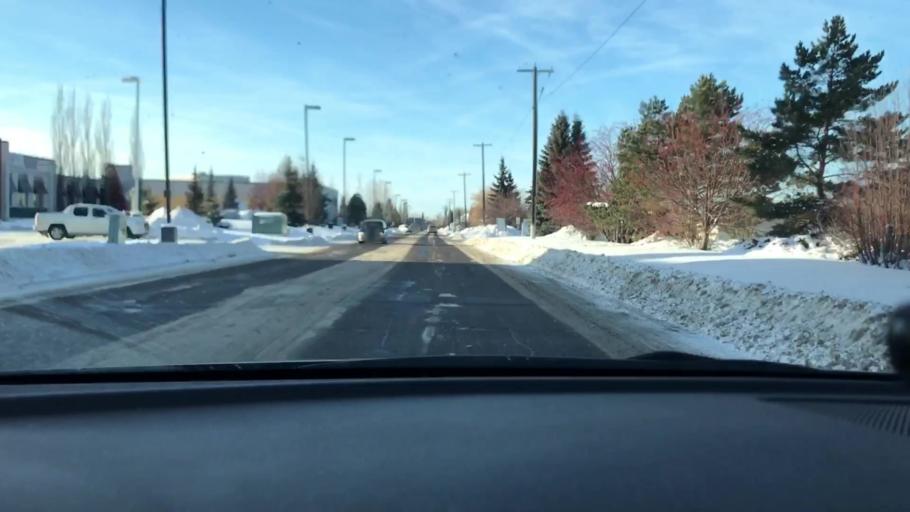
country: CA
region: Alberta
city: Edmonton
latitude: 53.4540
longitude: -113.4724
